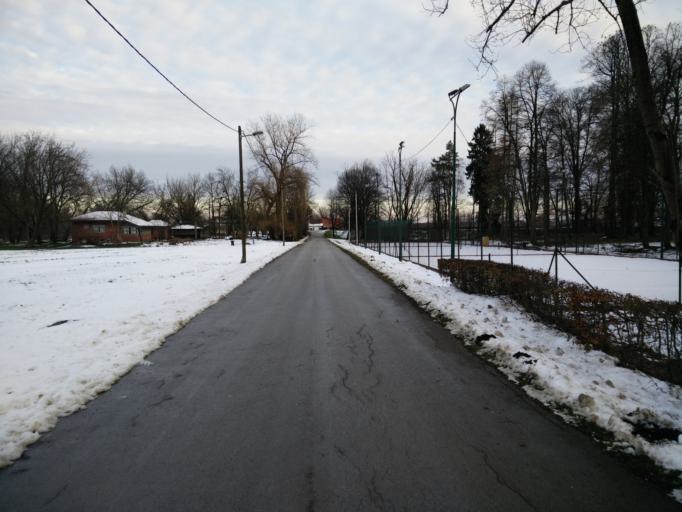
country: HR
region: Karlovacka
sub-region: Grad Karlovac
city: Karlovac
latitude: 45.4905
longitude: 15.5617
